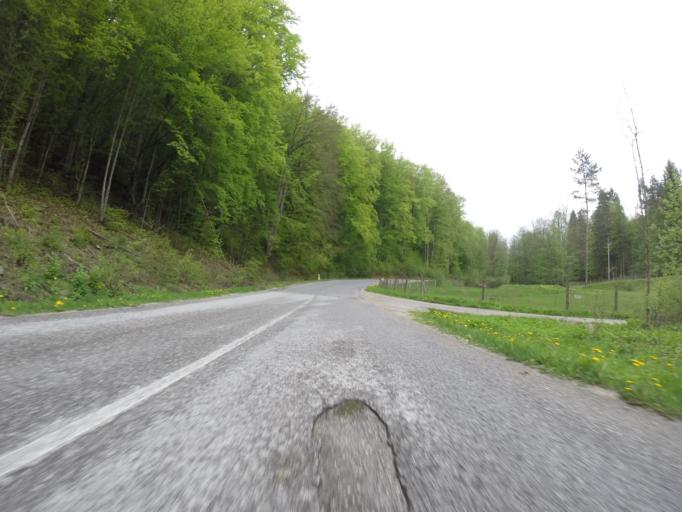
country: SK
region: Banskobystricky
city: Tisovec
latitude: 48.7169
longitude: 20.0041
